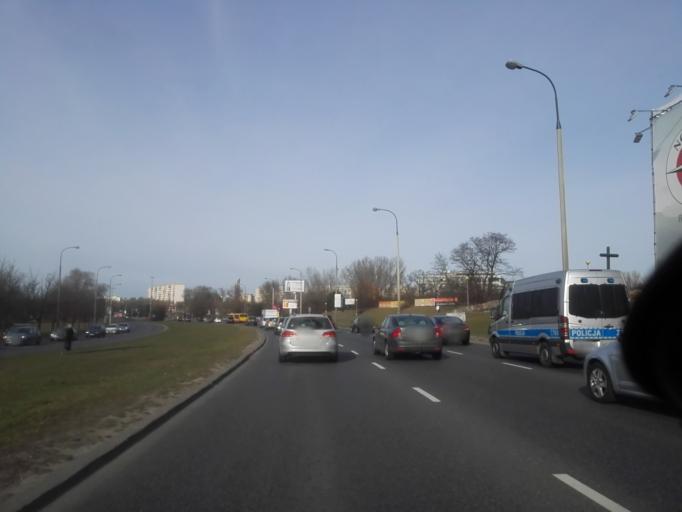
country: PL
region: Masovian Voivodeship
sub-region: Warszawa
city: Ursynow
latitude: 52.1719
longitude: 21.0428
